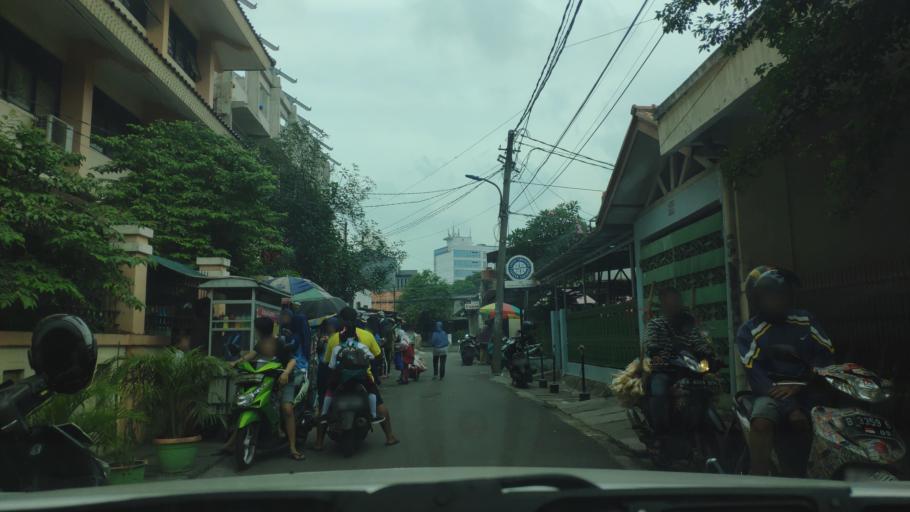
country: ID
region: Jakarta Raya
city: Jakarta
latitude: -6.1932
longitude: 106.7946
